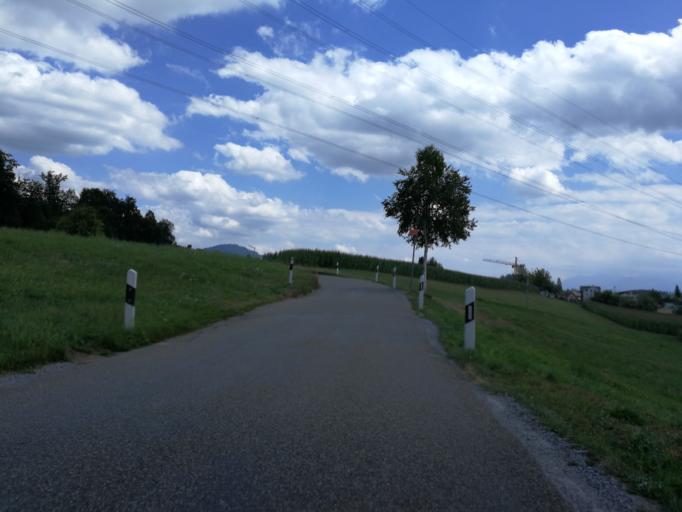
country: CH
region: Zurich
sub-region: Bezirk Hinwil
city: Gruet
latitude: 47.3131
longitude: 8.7751
